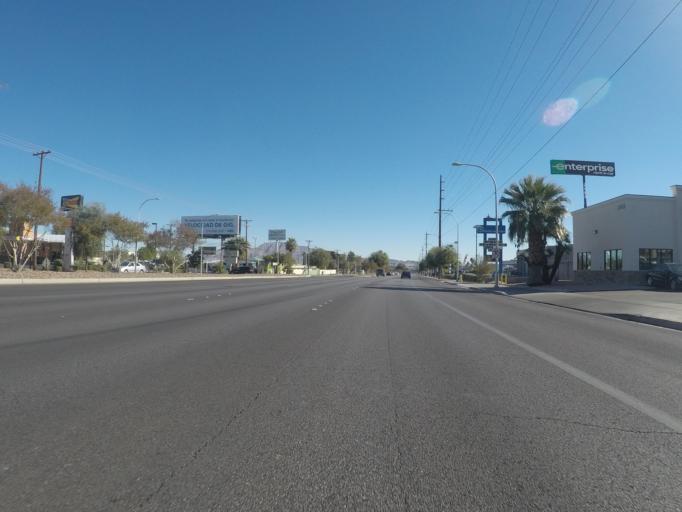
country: US
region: Nevada
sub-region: Clark County
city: Winchester
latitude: 36.1443
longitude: -115.1174
